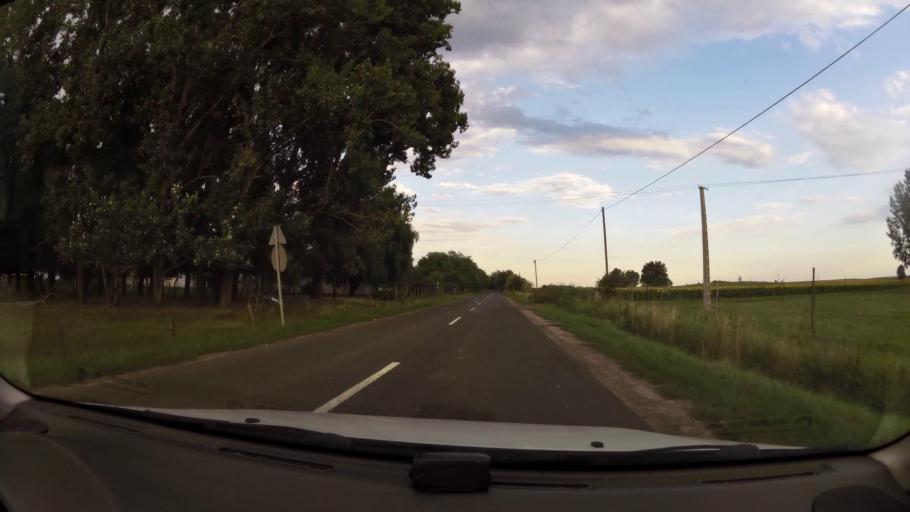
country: HU
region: Pest
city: Tapiobicske
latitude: 47.3528
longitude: 19.7039
